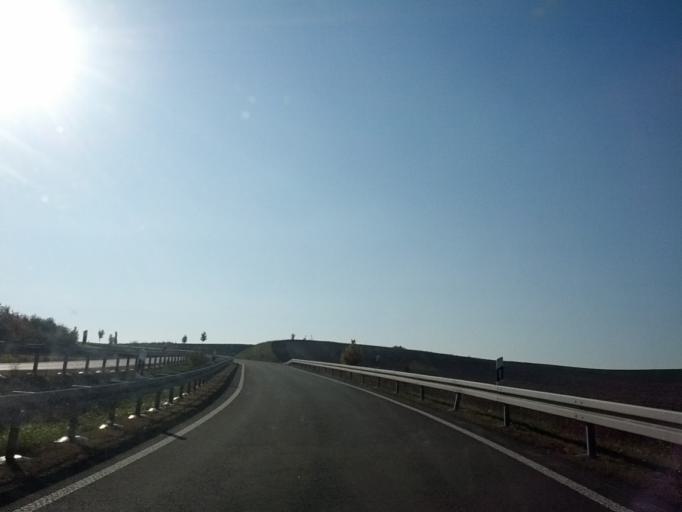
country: DE
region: Thuringia
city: Schwaara
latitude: 50.9029
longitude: 12.1237
